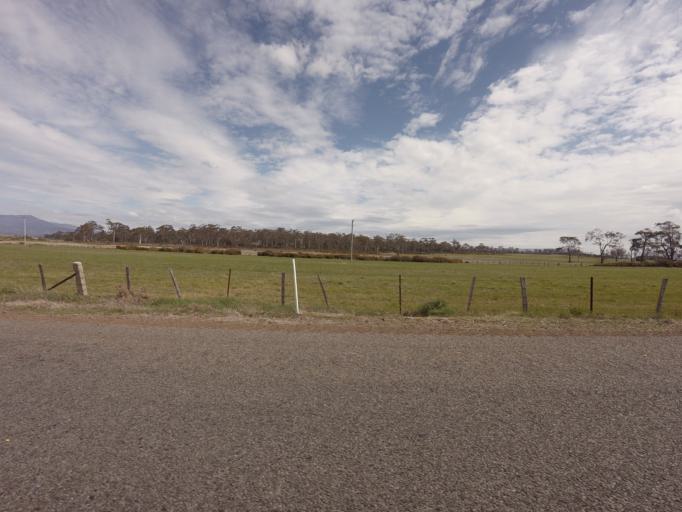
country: AU
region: Tasmania
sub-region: Northern Midlands
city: Longford
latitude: -41.7342
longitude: 147.1976
